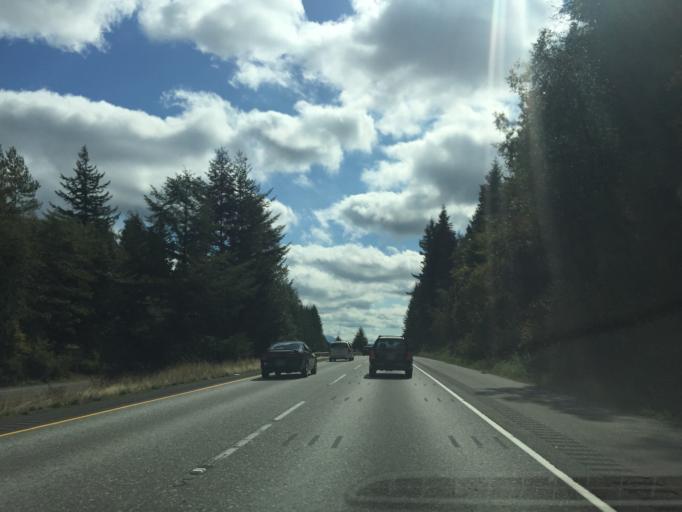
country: US
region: Washington
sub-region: Whatcom County
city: Sudden Valley
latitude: 48.6152
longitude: -122.3532
